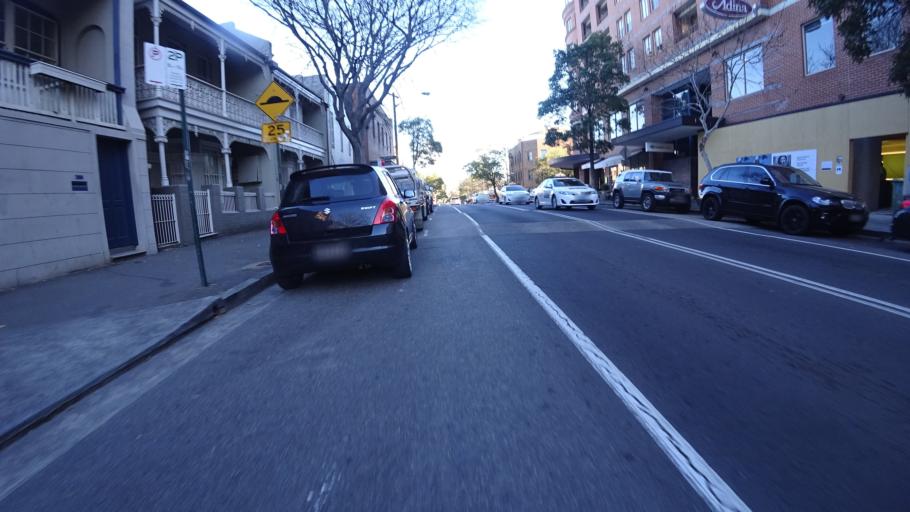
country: AU
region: New South Wales
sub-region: City of Sydney
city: Darlinghurst
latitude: -33.8839
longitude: 151.2144
